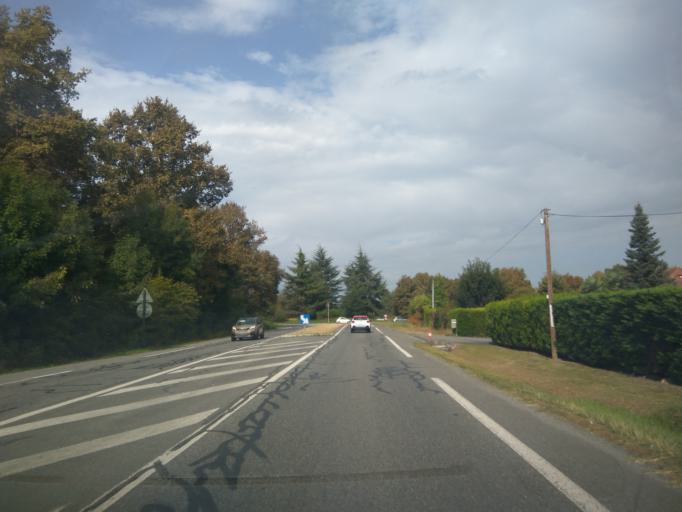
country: FR
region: Aquitaine
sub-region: Departement des Pyrenees-Atlantiques
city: Artiguelouve
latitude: 43.3149
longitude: -0.4559
